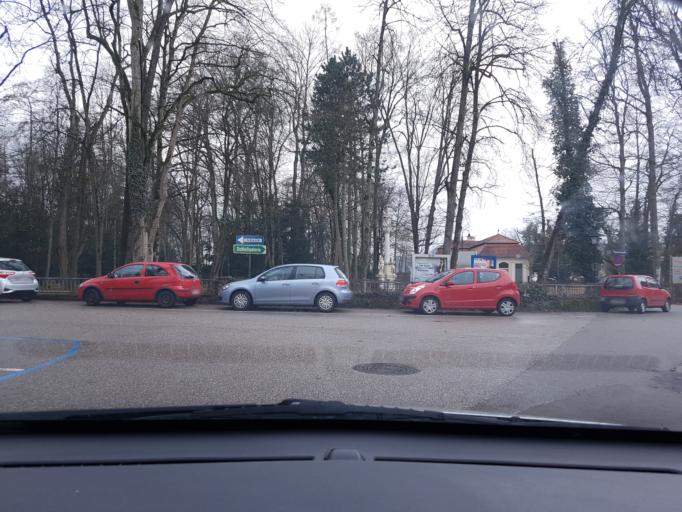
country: AT
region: Upper Austria
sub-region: Steyr Stadt
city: Steyr
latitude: 48.0411
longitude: 14.4187
